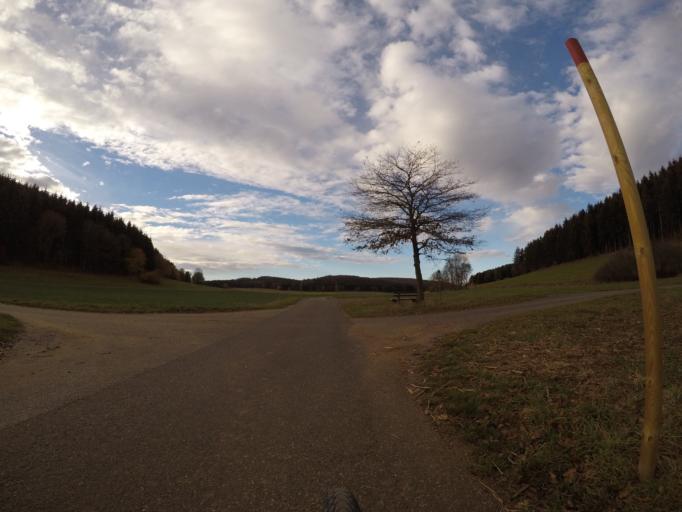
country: DE
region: Baden-Wuerttemberg
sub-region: Tuebingen Region
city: Sankt Johann
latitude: 48.4482
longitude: 9.3291
